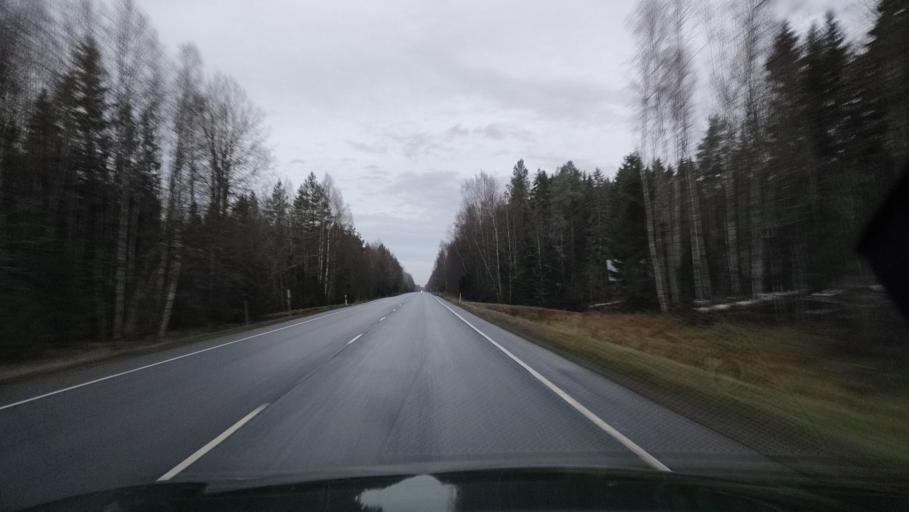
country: FI
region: Ostrobothnia
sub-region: Vaasa
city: Ristinummi
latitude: 63.0047
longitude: 21.7634
